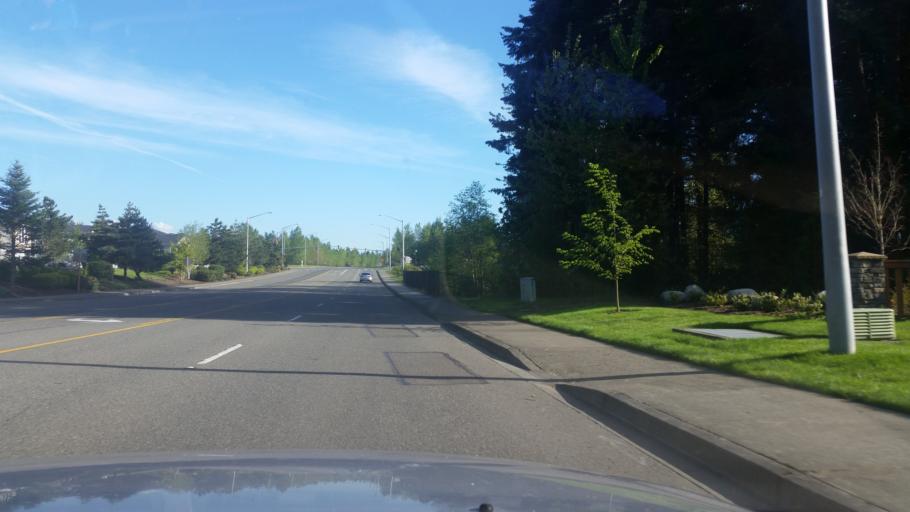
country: US
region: Washington
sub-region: Pierce County
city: South Hill
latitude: 47.0999
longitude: -122.2661
